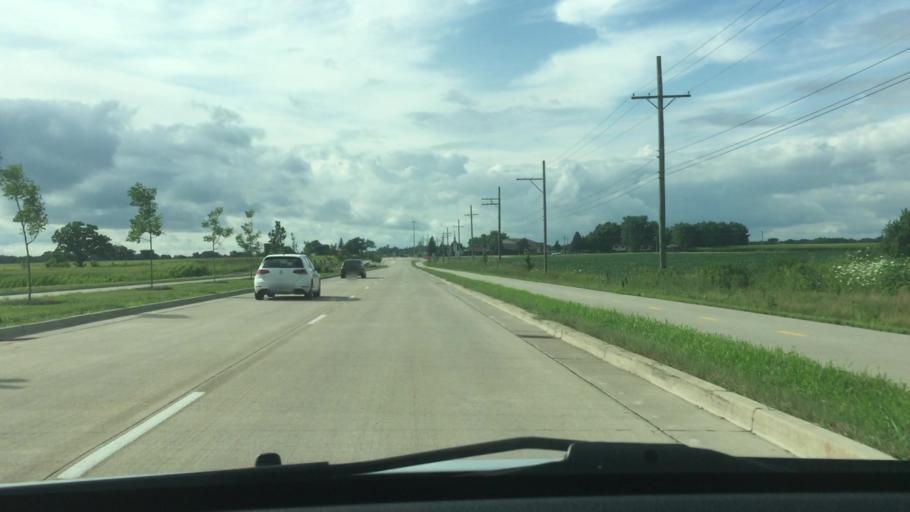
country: US
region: Illinois
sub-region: McHenry County
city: Lakewood
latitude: 42.2636
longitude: -88.3752
